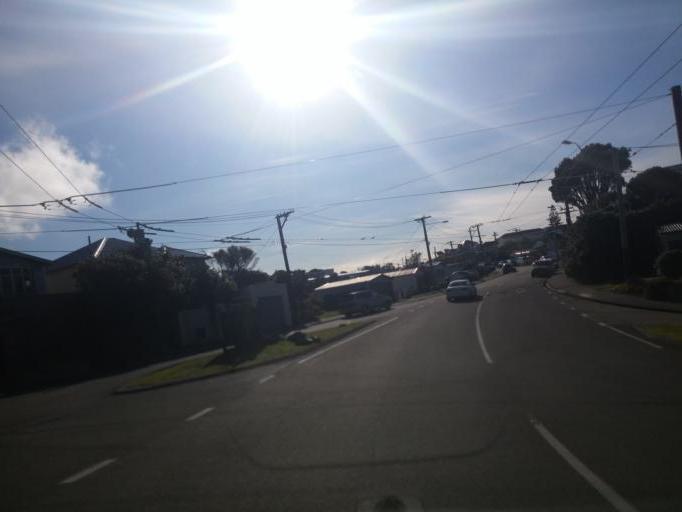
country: NZ
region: Wellington
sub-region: Wellington City
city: Brooklyn
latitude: -41.3181
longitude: 174.7640
